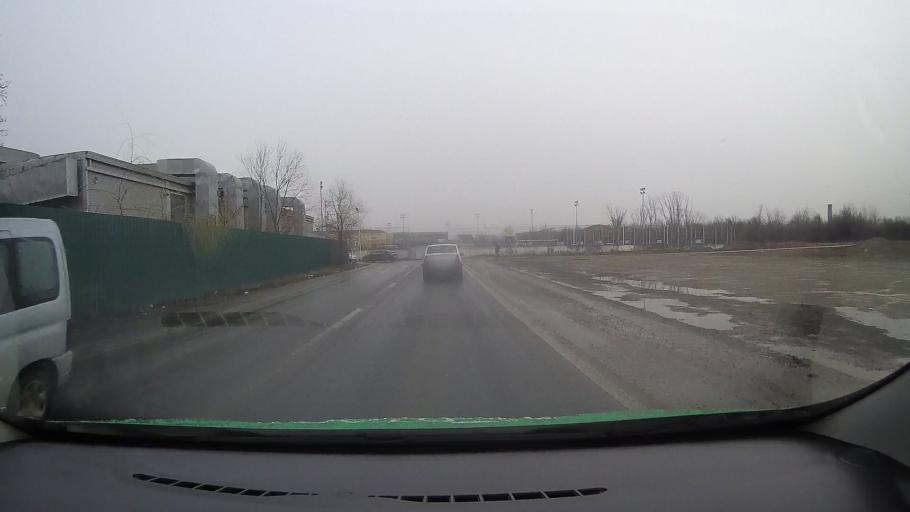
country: RO
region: Timis
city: Timisoara
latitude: 45.7403
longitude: 21.2498
